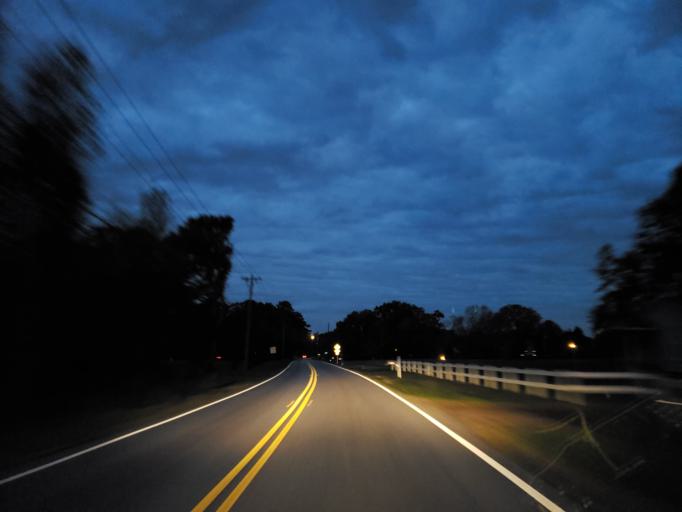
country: US
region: Georgia
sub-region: Cobb County
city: Powder Springs
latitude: 33.8904
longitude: -84.7073
